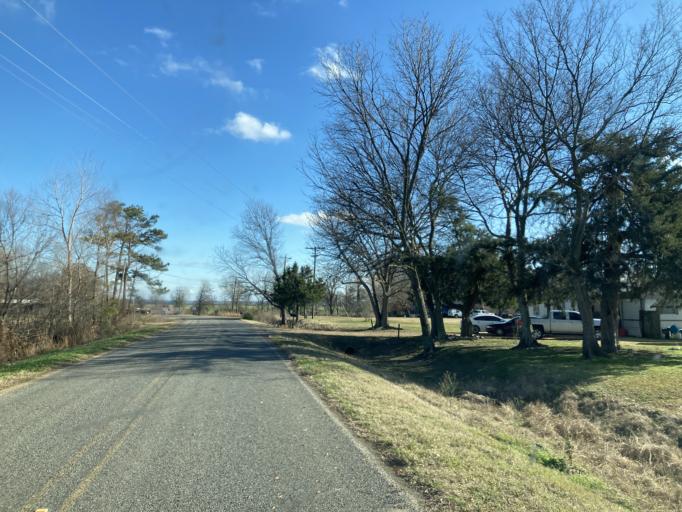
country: US
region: Mississippi
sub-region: Yazoo County
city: Yazoo City
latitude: 32.9262
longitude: -90.4697
